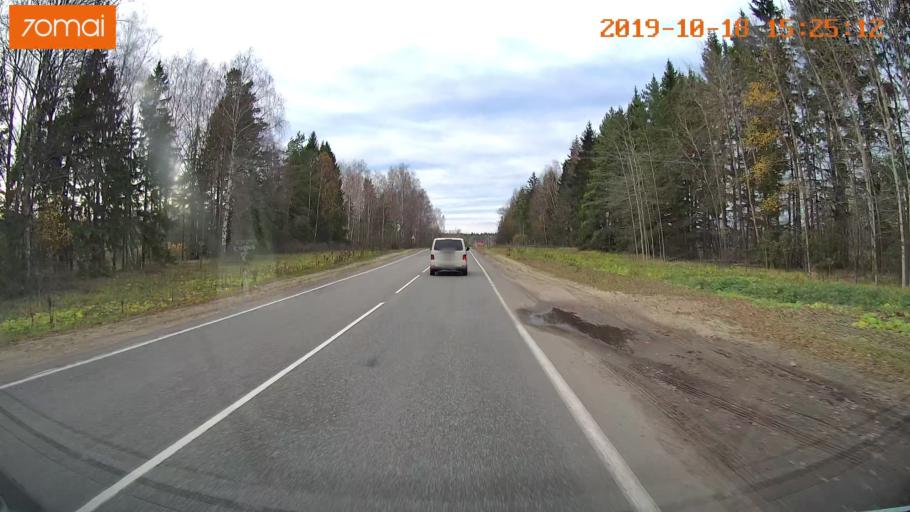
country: RU
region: Vladimir
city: Anopino
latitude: 55.7397
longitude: 40.7096
